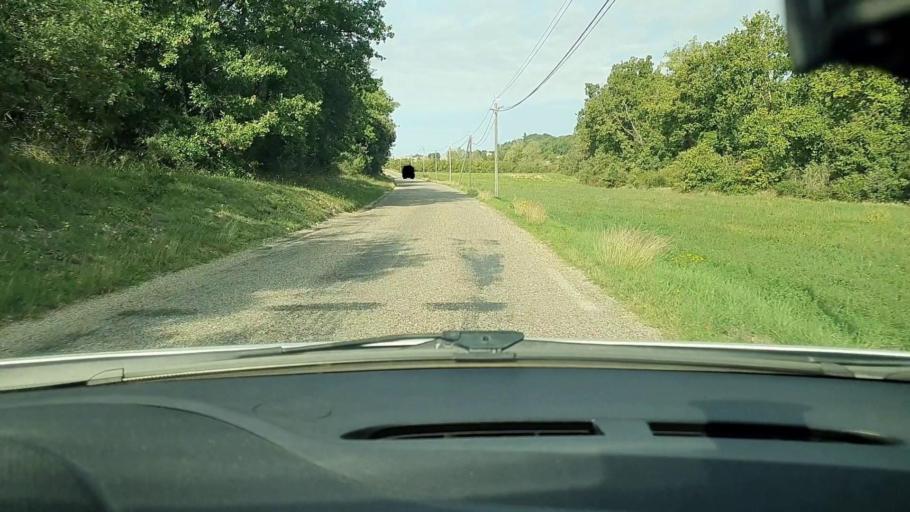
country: FR
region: Languedoc-Roussillon
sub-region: Departement du Gard
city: Goudargues
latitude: 44.1433
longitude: 4.3895
